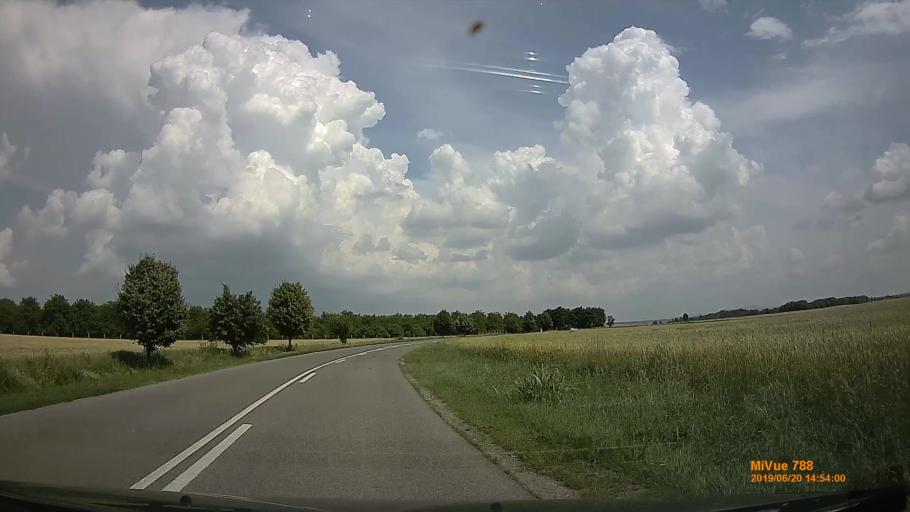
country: HU
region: Baranya
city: Kozarmisleny
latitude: 46.0027
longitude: 18.2386
